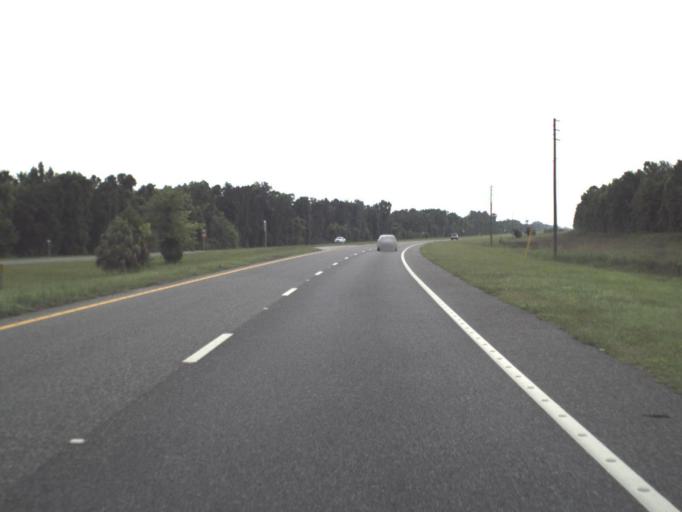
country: US
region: Florida
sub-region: Levy County
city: Inglis
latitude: 29.1881
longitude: -82.6829
